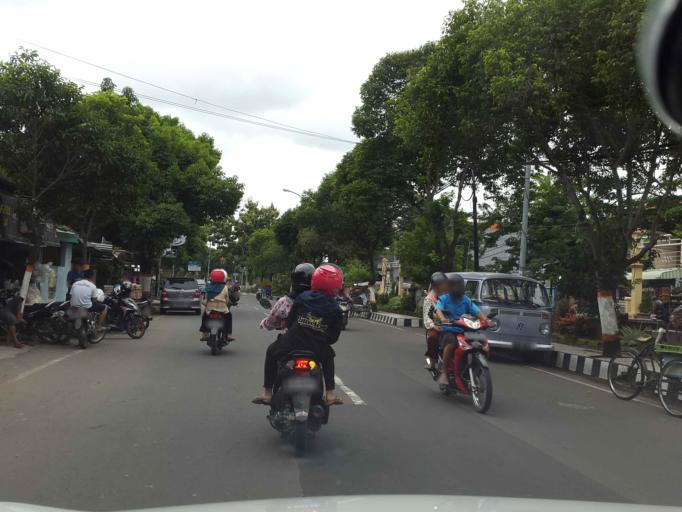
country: ID
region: East Java
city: Mojokerto
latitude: -7.4666
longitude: 112.4469
